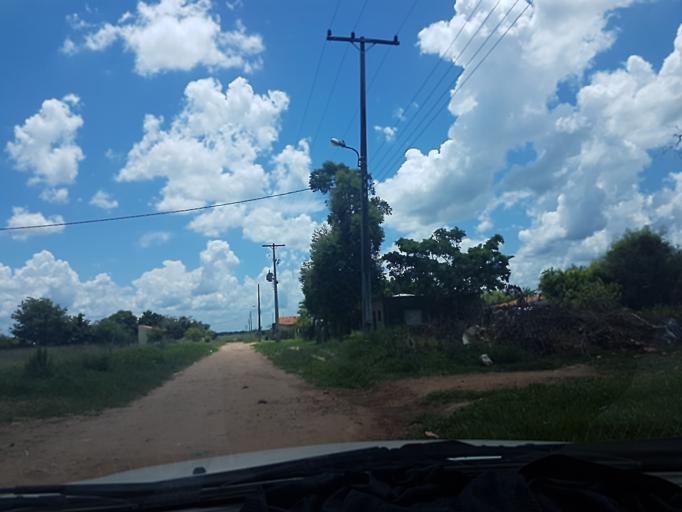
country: PY
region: Central
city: Limpio
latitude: -25.1377
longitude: -57.4854
